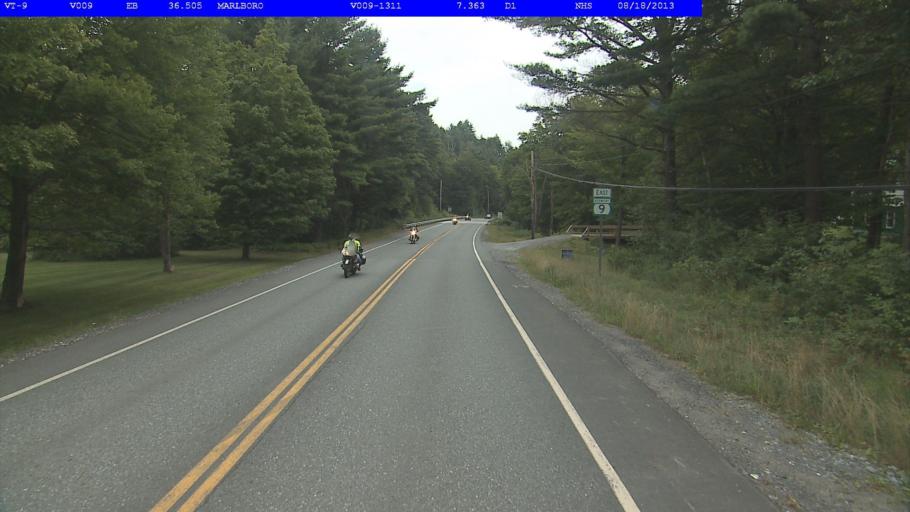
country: US
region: Vermont
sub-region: Windham County
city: West Brattleboro
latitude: 42.8782
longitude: -72.6936
